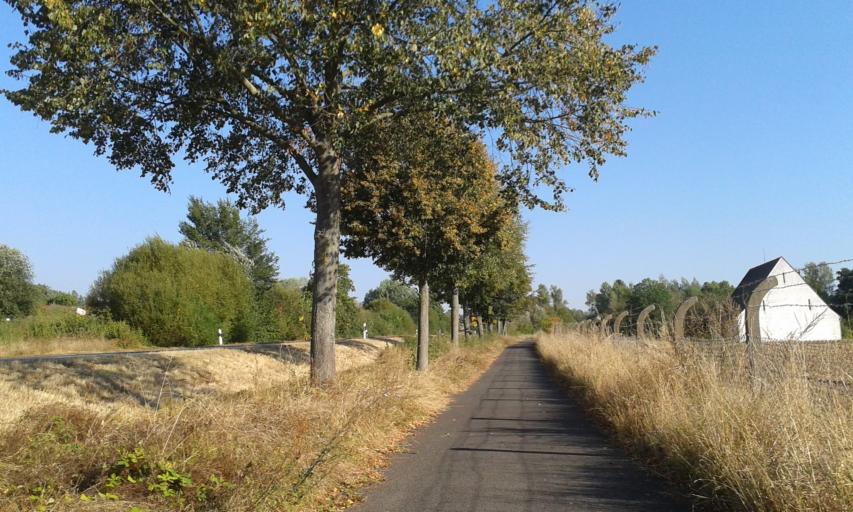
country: DE
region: Bavaria
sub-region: Upper Franconia
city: Bamberg
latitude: 49.8676
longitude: 10.8832
